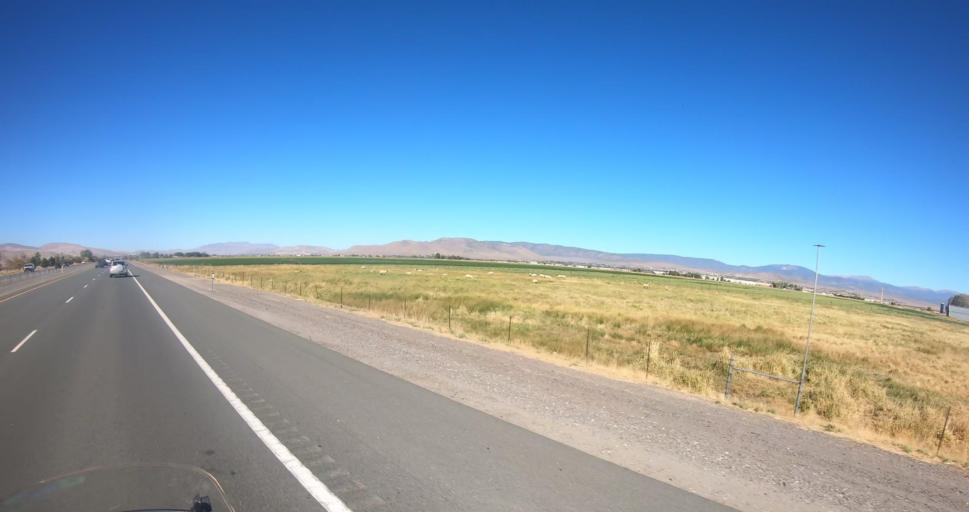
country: US
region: Nevada
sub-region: Douglas County
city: Minden
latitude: 39.0061
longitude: -119.7791
